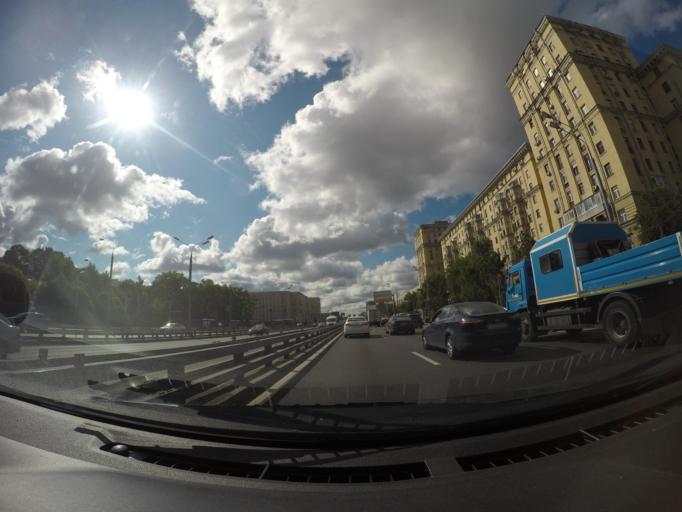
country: RU
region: Moskovskaya
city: Koptevo
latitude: 55.8200
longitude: 37.4971
